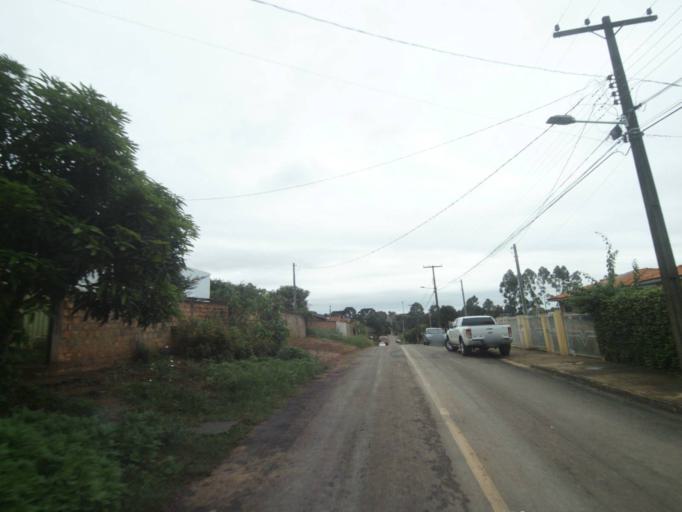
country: BR
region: Parana
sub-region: Telemaco Borba
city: Telemaco Borba
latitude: -24.3170
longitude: -50.6537
